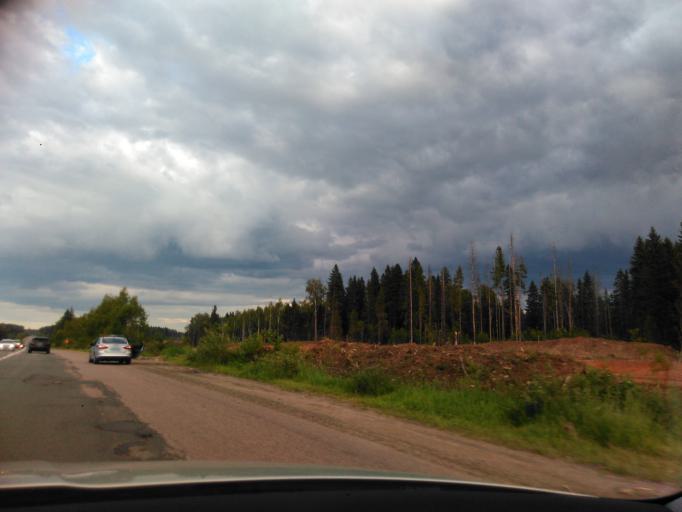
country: RU
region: Moskovskaya
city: Solnechnogorsk
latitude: 56.1424
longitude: 36.9947
